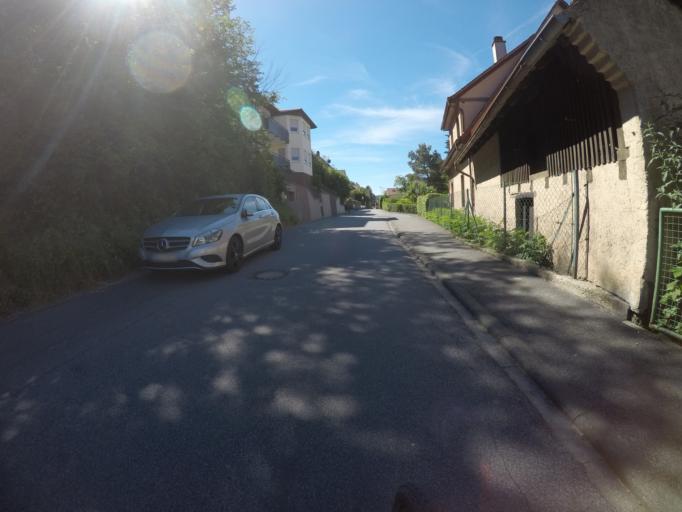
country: DE
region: Baden-Wuerttemberg
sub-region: Karlsruhe Region
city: Konigsbach-Stein
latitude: 48.9492
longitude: 8.6257
